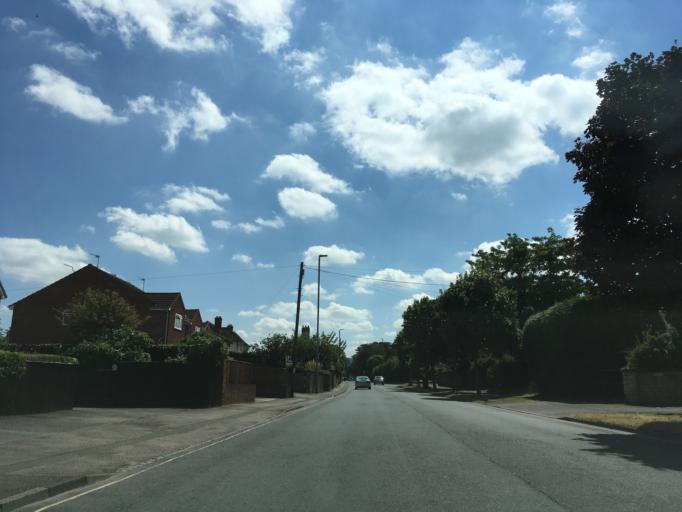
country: GB
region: England
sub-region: Gloucestershire
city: Barnwood
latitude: 51.8549
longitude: -2.1859
